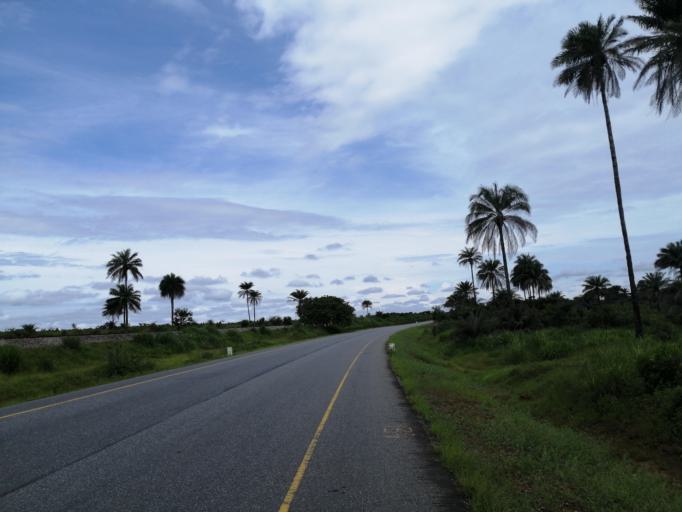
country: SL
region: Northern Province
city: Port Loko
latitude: 8.7464
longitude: -12.9225
